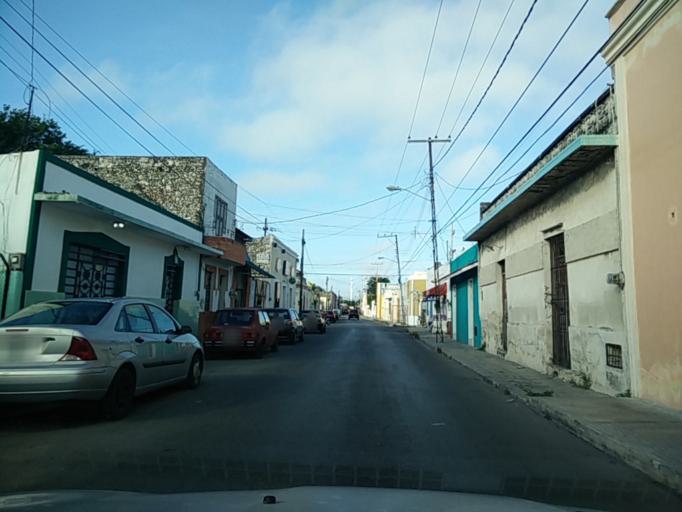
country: MX
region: Yucatan
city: Merida
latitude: 20.9673
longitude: -89.6364
